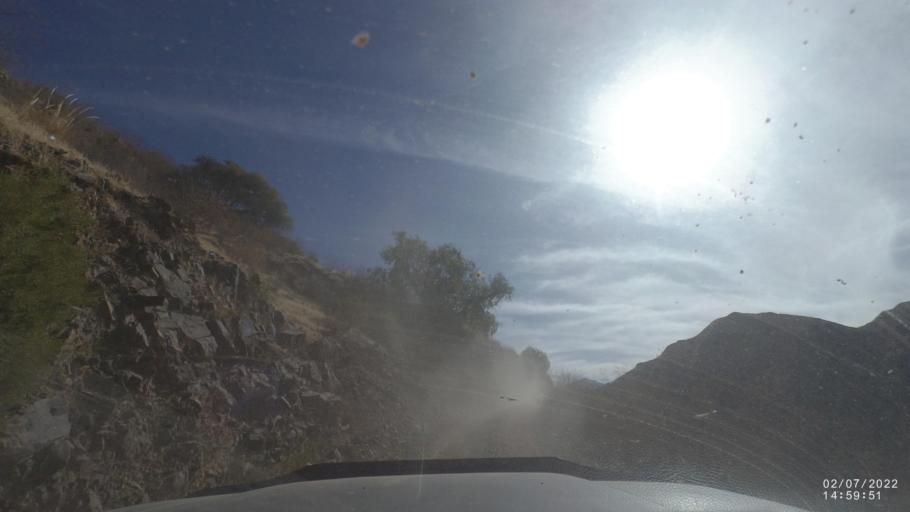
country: BO
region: Cochabamba
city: Irpa Irpa
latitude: -17.8526
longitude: -66.4409
